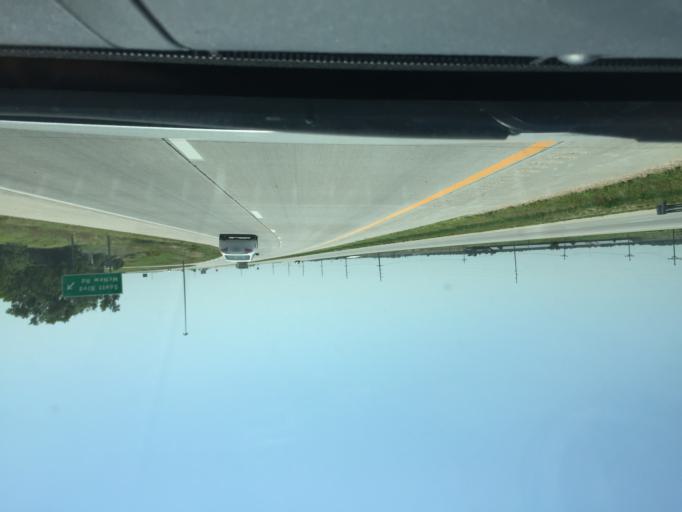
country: US
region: Kansas
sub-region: Reno County
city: South Hutchinson
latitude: 38.0155
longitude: -97.9148
